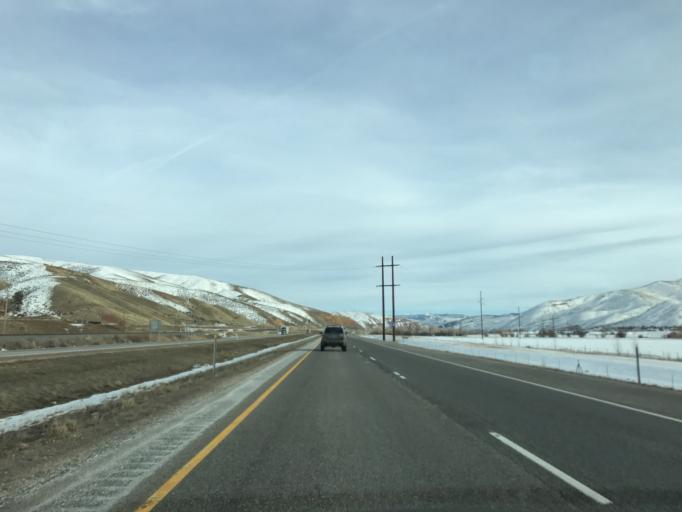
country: US
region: Utah
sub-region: Summit County
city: Coalville
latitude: 41.0119
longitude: -111.4848
